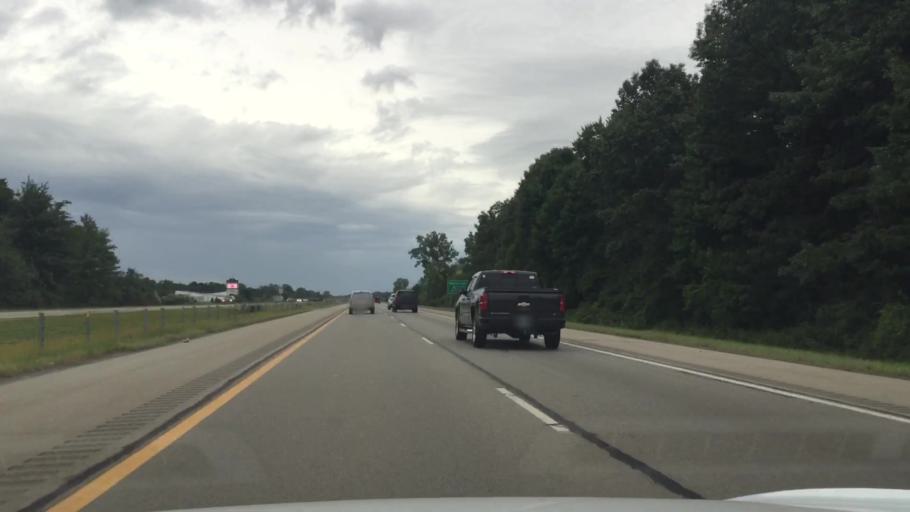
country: US
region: Michigan
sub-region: Macomb County
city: New Baltimore
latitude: 42.7272
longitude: -82.7421
